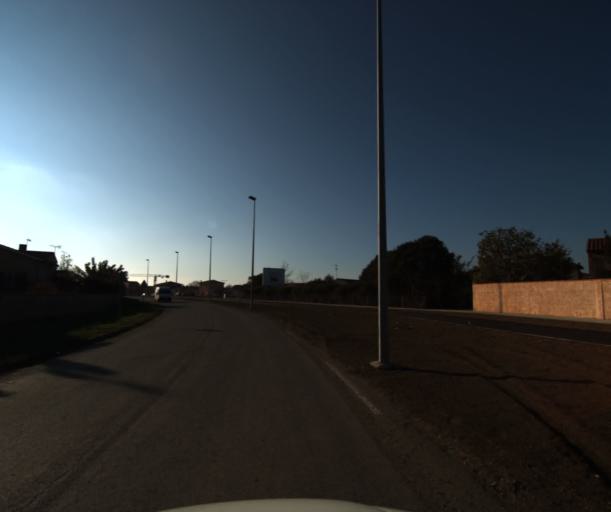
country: FR
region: Midi-Pyrenees
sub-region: Departement de la Haute-Garonne
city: Colomiers
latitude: 43.6244
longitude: 1.3317
